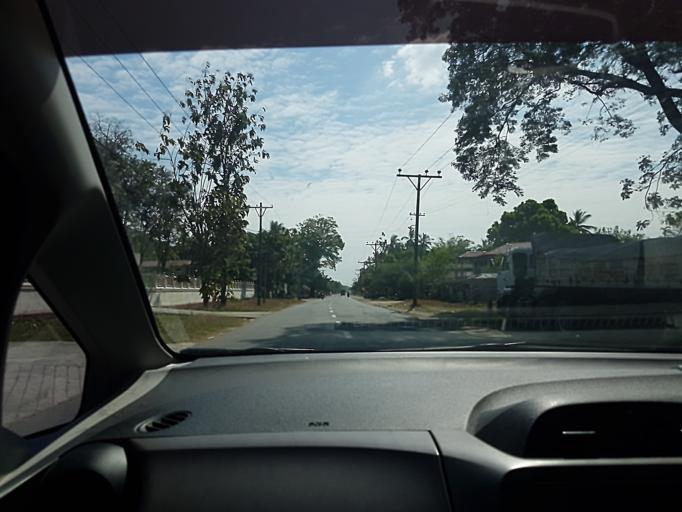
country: MM
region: Mon
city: Thaton
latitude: 16.7050
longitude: 97.4229
